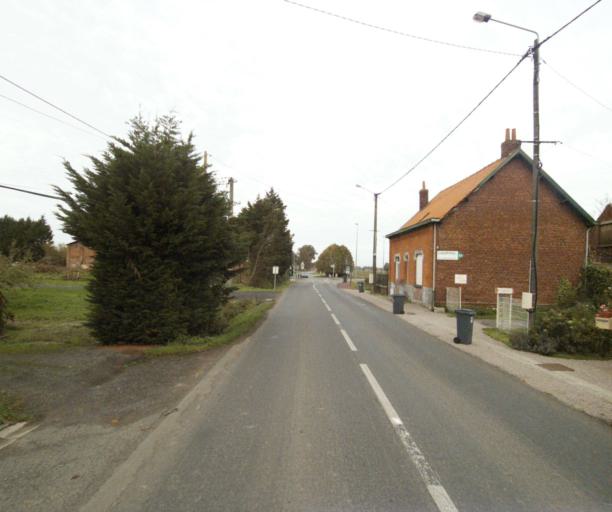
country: FR
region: Nord-Pas-de-Calais
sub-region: Departement du Nord
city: Aubers
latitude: 50.5972
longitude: 2.8113
